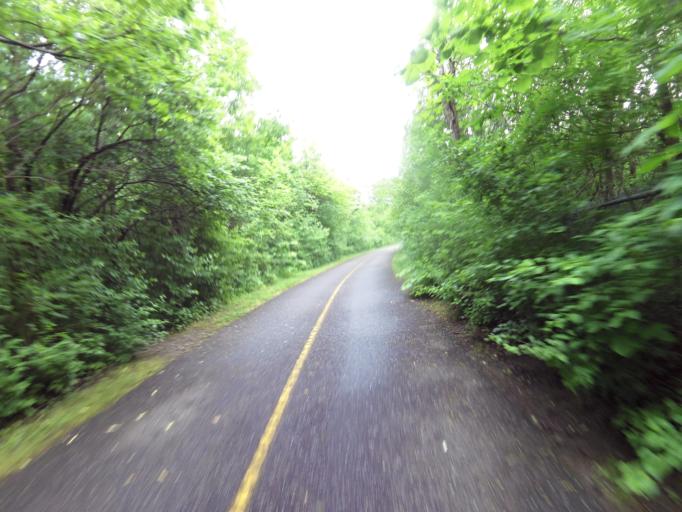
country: CA
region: Ontario
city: Ottawa
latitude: 45.3721
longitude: -75.7405
